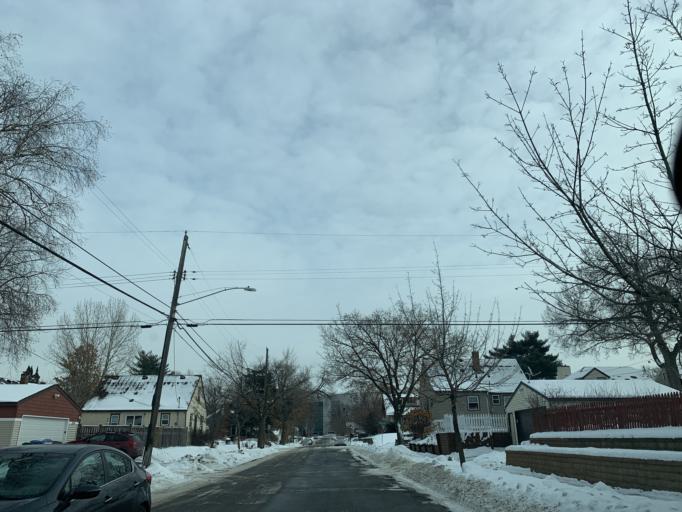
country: US
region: Minnesota
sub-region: Hennepin County
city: Richfield
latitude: 44.9018
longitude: -93.2112
